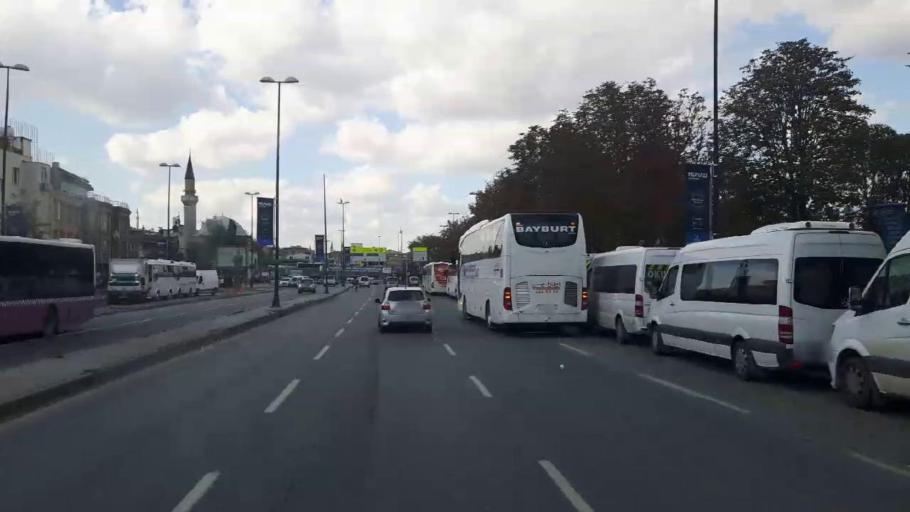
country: TR
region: Istanbul
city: Eminoenue
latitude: 41.0206
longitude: 28.9635
